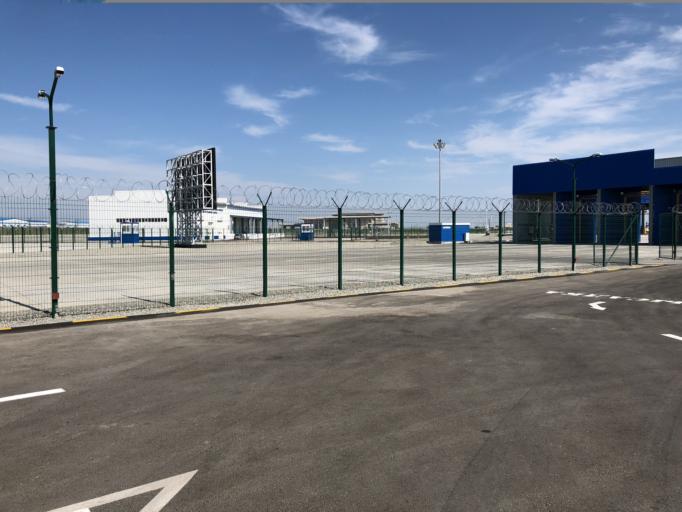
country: KZ
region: Almaty Oblysy
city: Zharkent
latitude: 44.1579
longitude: 80.3966
